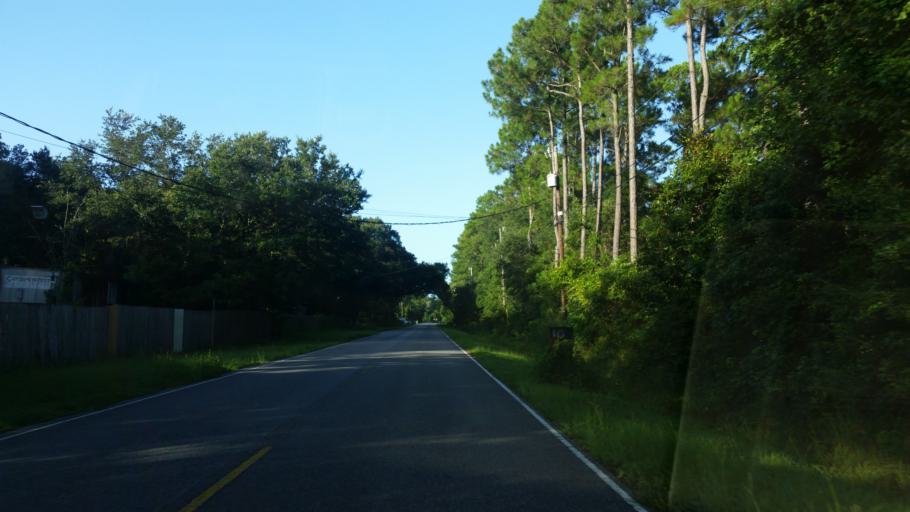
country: US
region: Florida
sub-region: Escambia County
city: Myrtle Grove
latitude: 30.4115
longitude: -87.3224
